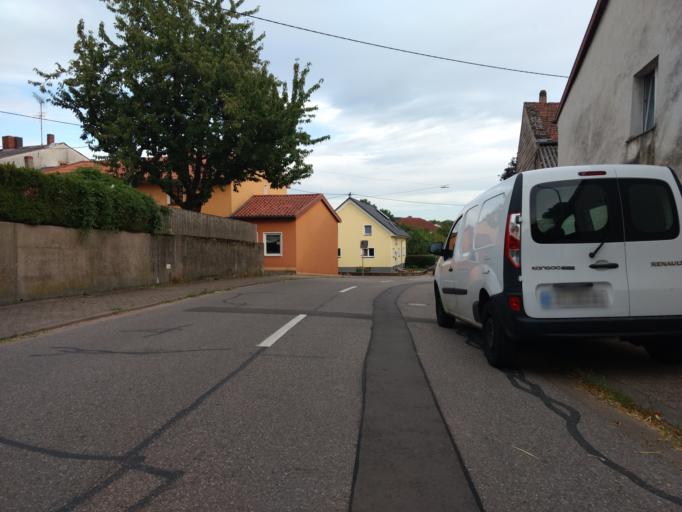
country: FR
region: Lorraine
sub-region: Departement de la Moselle
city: Bouzonville
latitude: 49.3240
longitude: 6.6054
